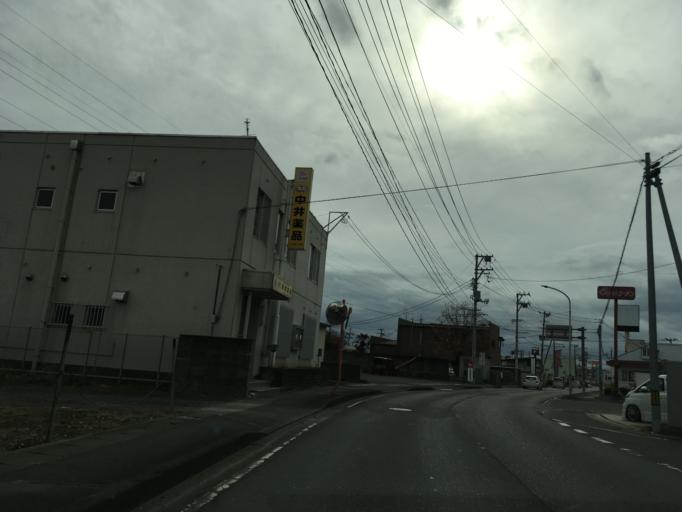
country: JP
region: Miyagi
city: Wakuya
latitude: 38.6912
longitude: 141.2063
